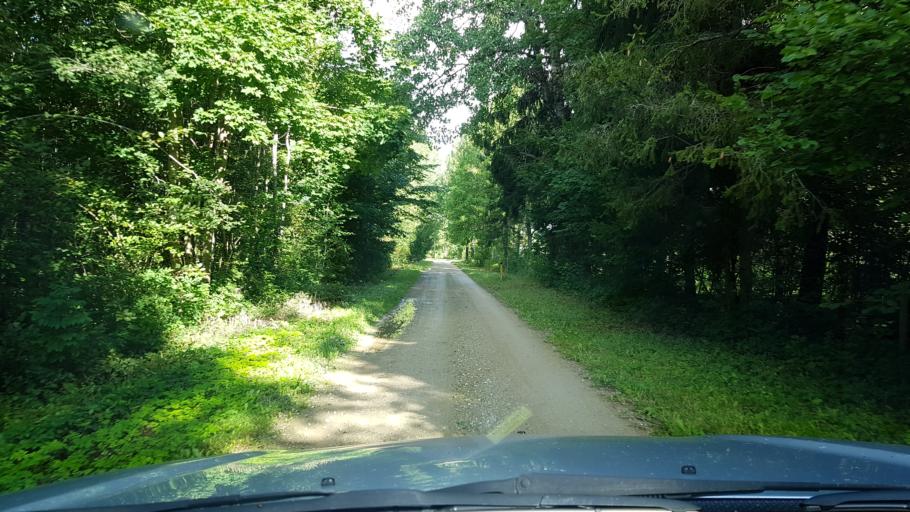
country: EE
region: Harju
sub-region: Raasiku vald
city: Arukula
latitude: 59.2595
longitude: 25.0978
